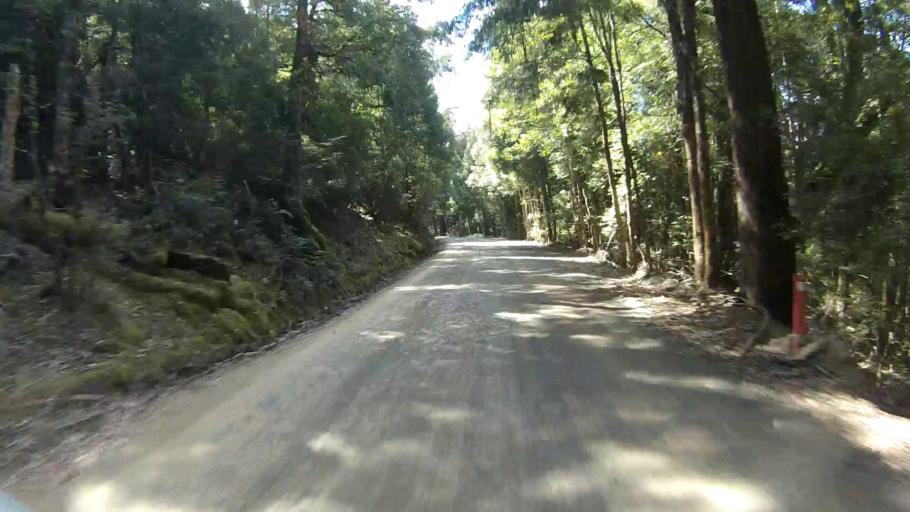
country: AU
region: Tasmania
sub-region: Derwent Valley
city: New Norfolk
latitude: -42.6811
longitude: 146.6792
